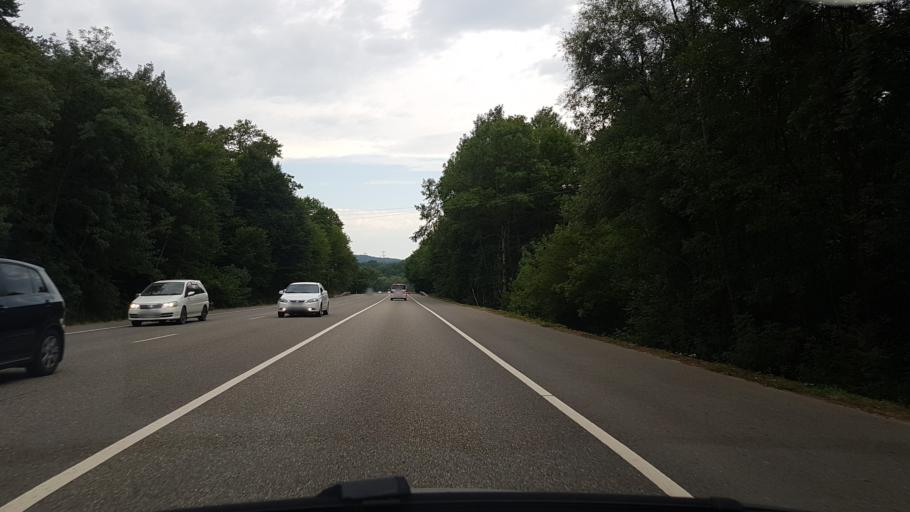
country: RU
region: Krasnodarskiy
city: Dzhubga
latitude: 44.4115
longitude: 38.7405
